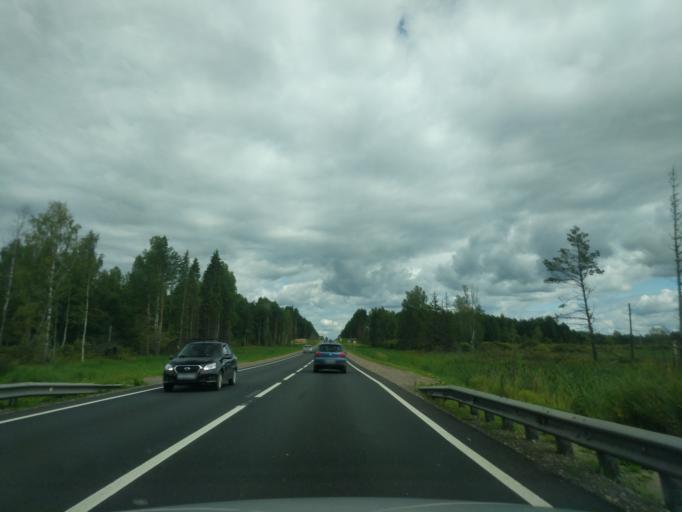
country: RU
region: Jaroslavl
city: Nekrasovskoye
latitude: 57.5749
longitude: 40.2743
